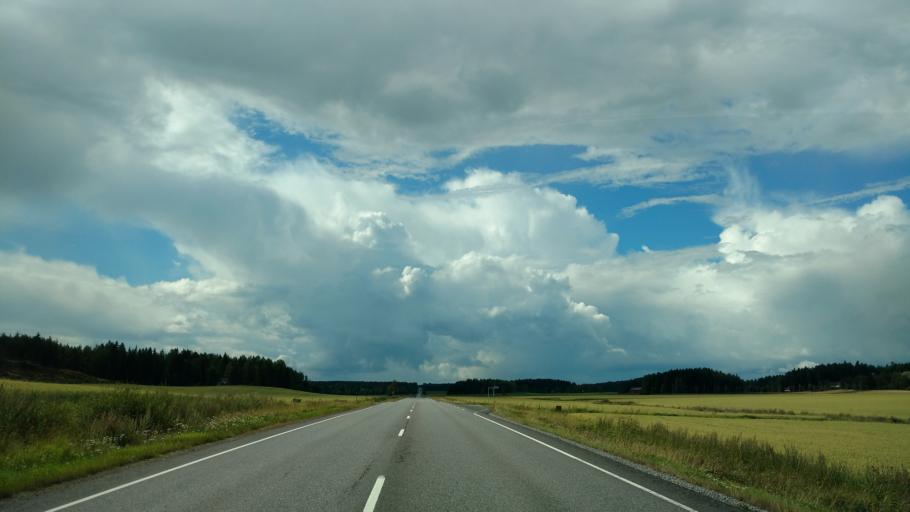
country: FI
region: Varsinais-Suomi
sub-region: Turku
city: Sauvo
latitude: 60.3893
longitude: 22.8750
